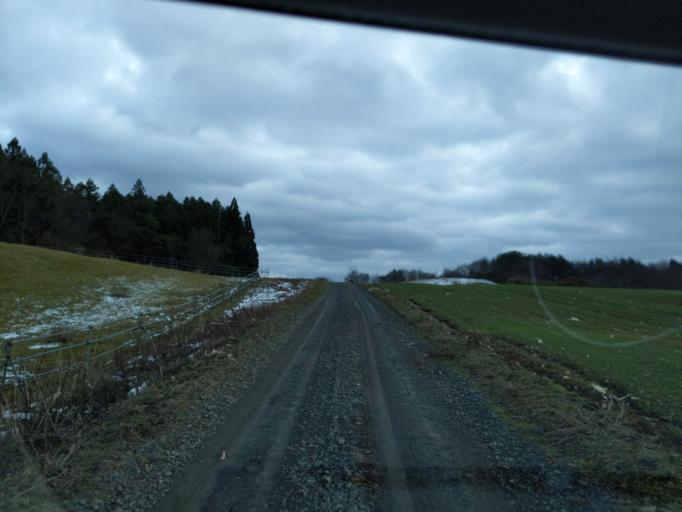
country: JP
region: Iwate
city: Ichinoseki
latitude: 38.9801
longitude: 141.0137
